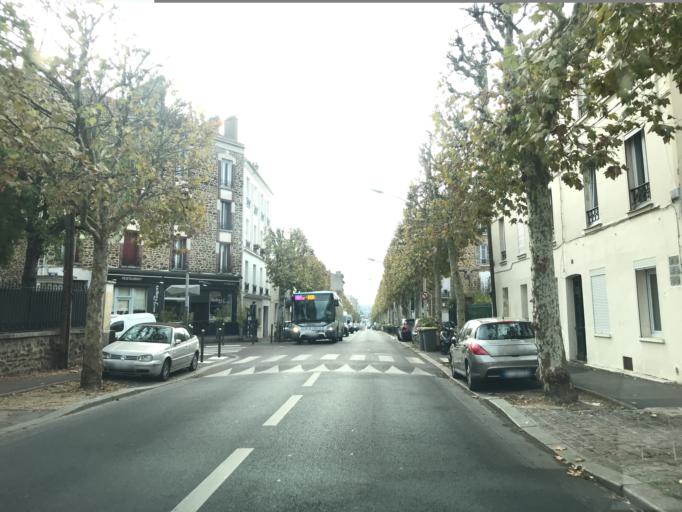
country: FR
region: Ile-de-France
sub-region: Departement du Val-de-Marne
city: Le Perreux-sur-Marne
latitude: 48.8457
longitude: 2.5003
